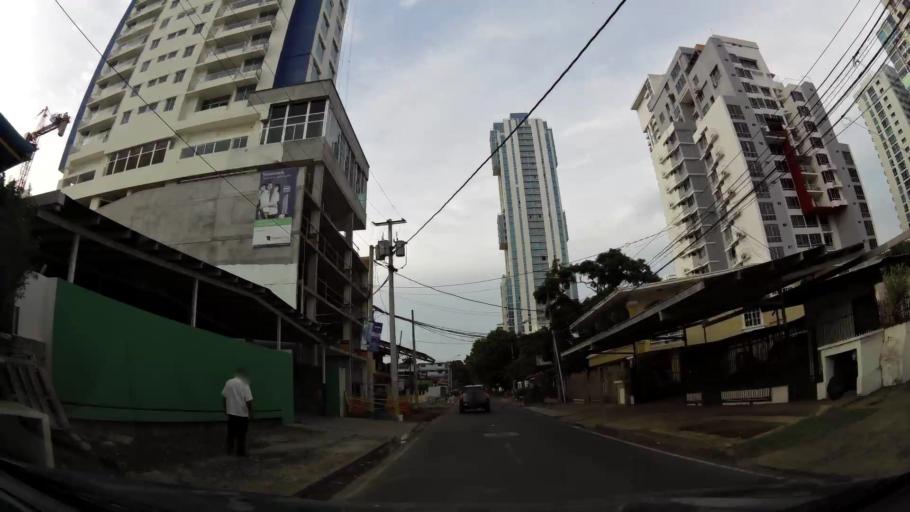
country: PA
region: Panama
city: Panama
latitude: 8.9938
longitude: -79.5069
